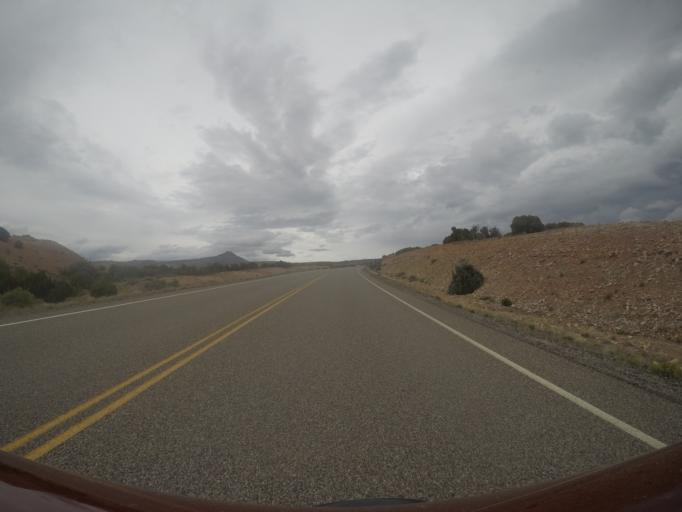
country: US
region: Wyoming
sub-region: Big Horn County
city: Lovell
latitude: 44.9774
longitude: -108.2626
